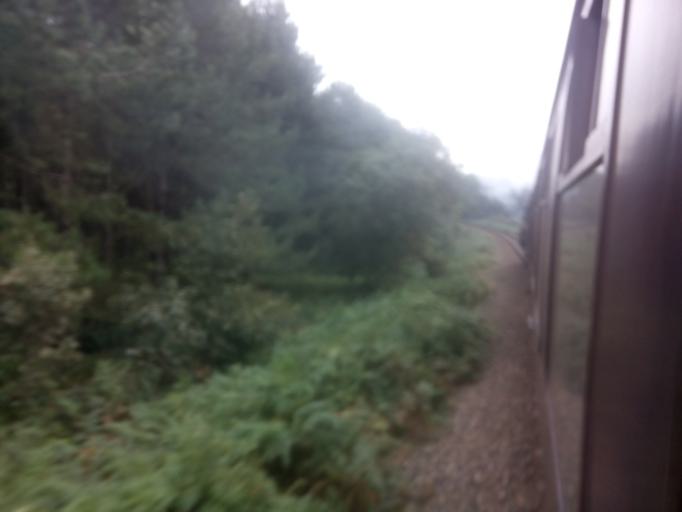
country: GB
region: England
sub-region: Norfolk
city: Sheringham
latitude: 52.9270
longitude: 1.1188
